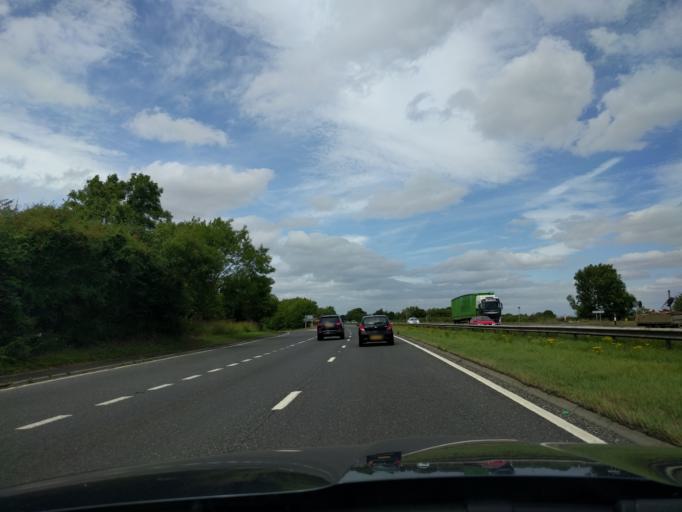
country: GB
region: England
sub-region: Northumberland
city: Stannington
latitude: 55.1347
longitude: -1.6782
